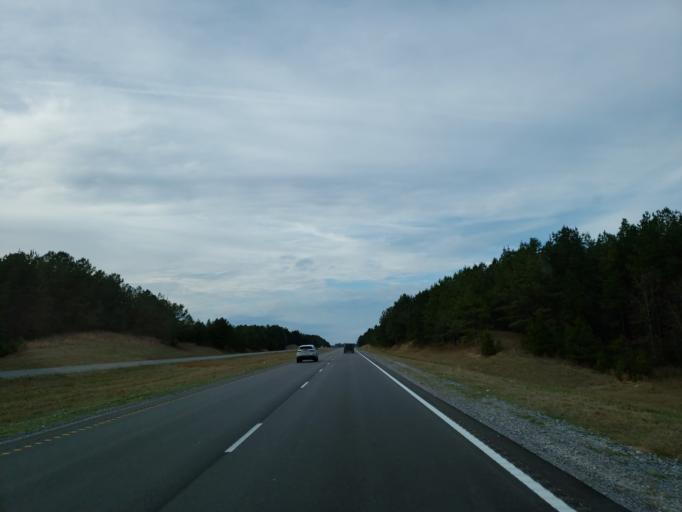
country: US
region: Mississippi
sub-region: Clarke County
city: Quitman
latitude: 32.0831
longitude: -88.6937
